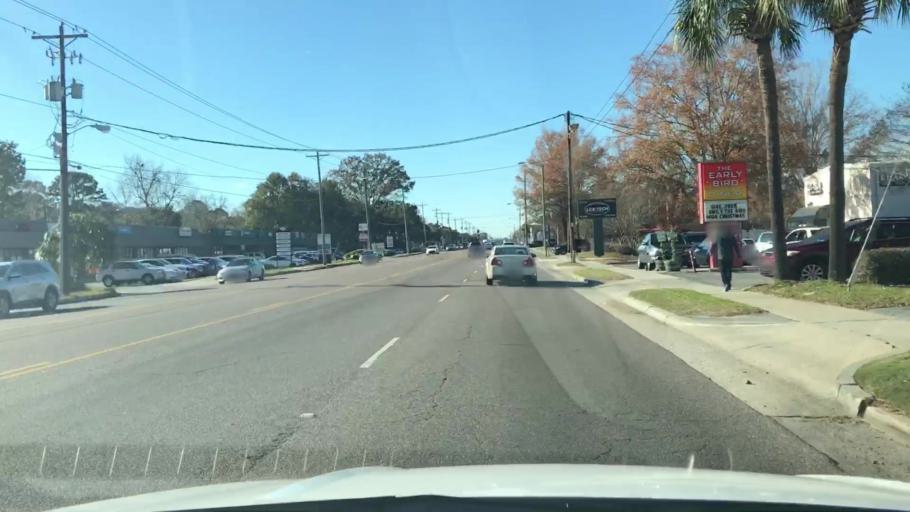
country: US
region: South Carolina
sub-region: Charleston County
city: North Charleston
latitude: 32.7870
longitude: -80.0138
